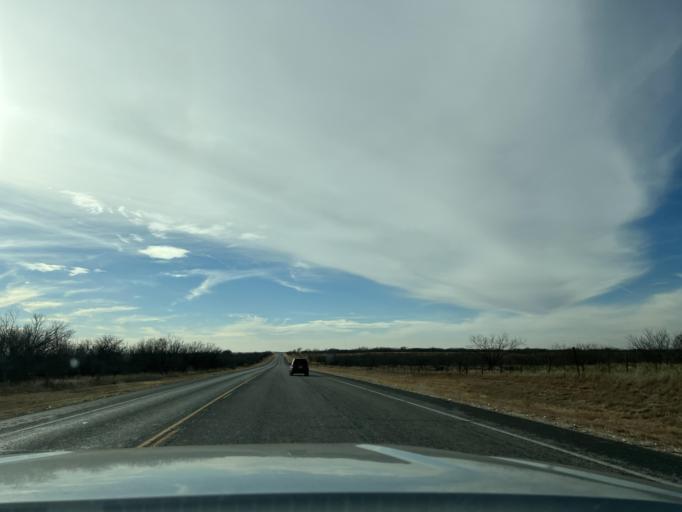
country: US
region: Texas
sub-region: Fisher County
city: Roby
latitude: 32.7556
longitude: -100.3307
